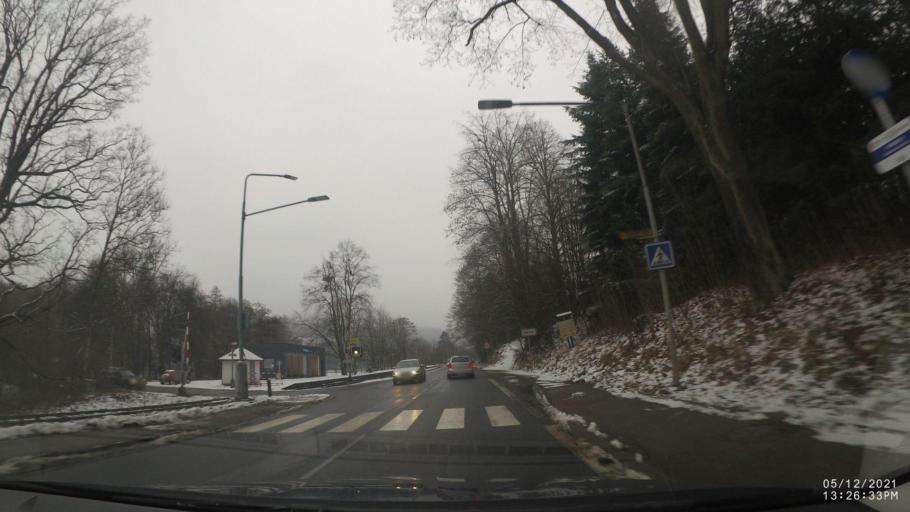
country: CZ
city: Hronov
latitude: 50.4899
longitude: 16.1860
